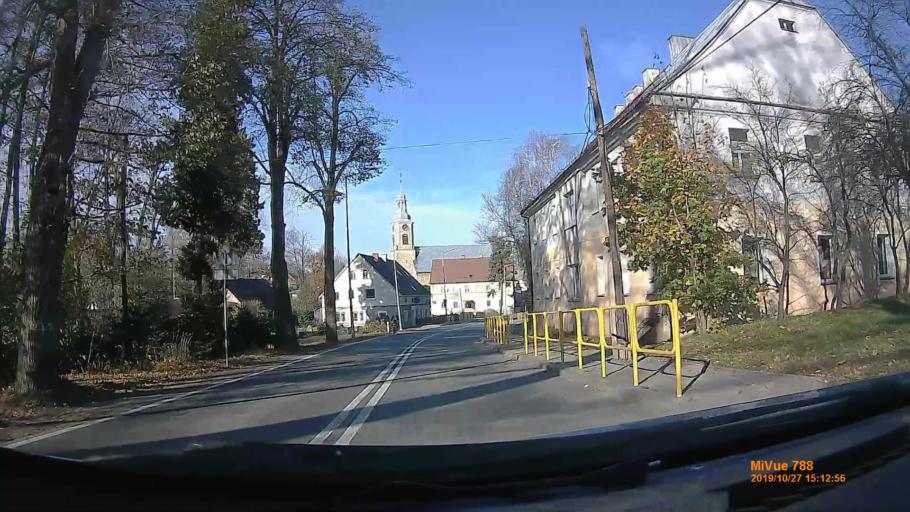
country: PL
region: Lower Silesian Voivodeship
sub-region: Powiat klodzki
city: Miedzylesie
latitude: 50.2135
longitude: 16.6798
